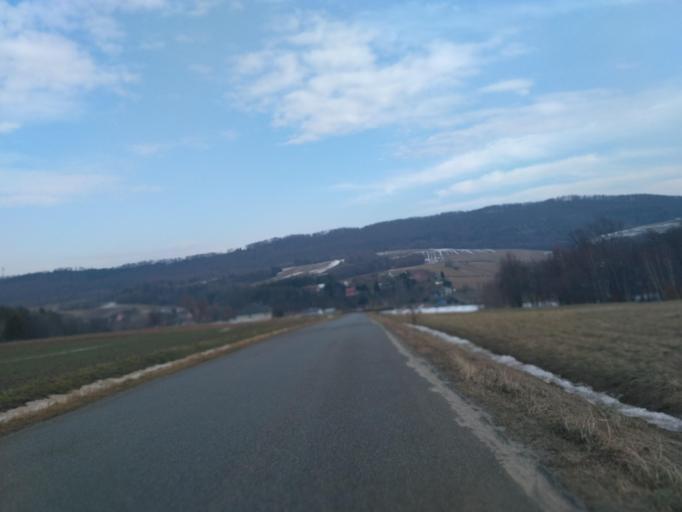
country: PL
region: Subcarpathian Voivodeship
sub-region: Powiat brzozowski
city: Grabownica Starzenska
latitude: 49.6408
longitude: 22.0938
